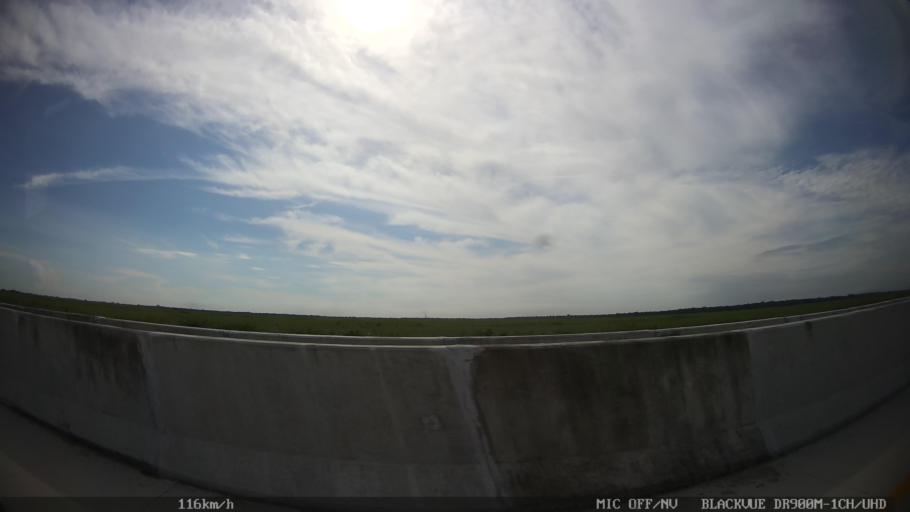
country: ID
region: North Sumatra
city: Binjai
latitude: 3.6663
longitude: 98.5332
